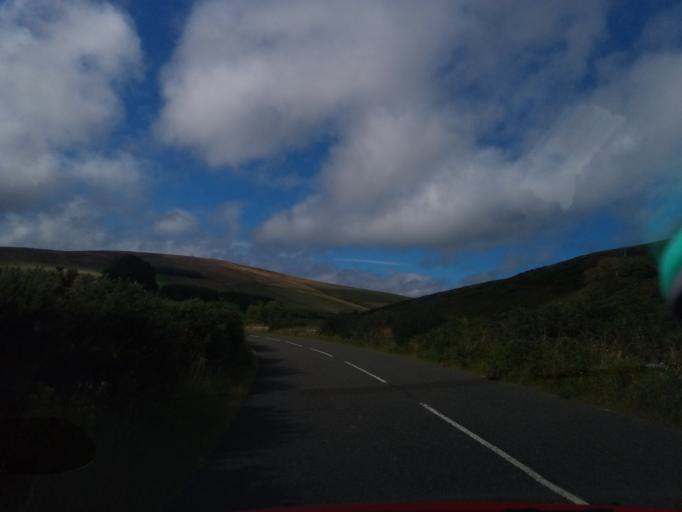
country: GB
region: Scotland
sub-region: East Lothian
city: Dunbar
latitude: 55.8604
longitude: -2.5056
